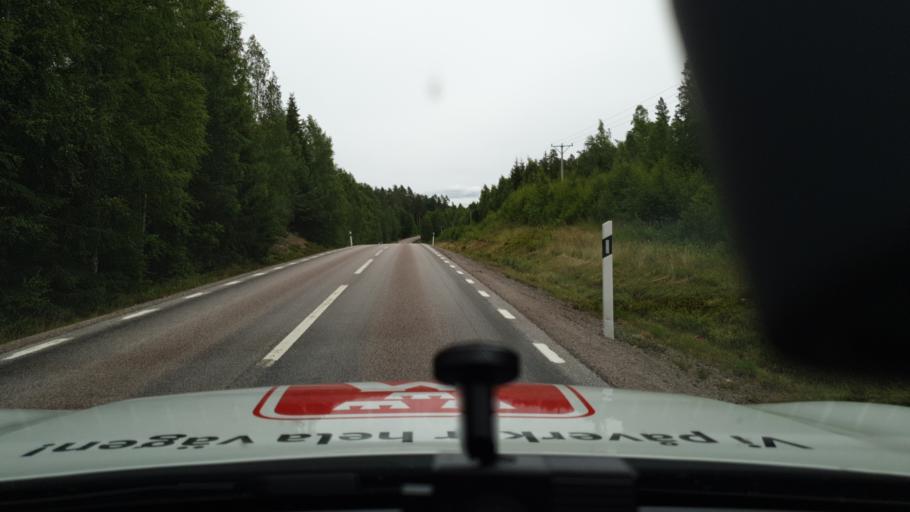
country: SE
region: Vaermland
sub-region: Hagfors Kommun
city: Ekshaerad
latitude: 60.1857
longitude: 13.3274
